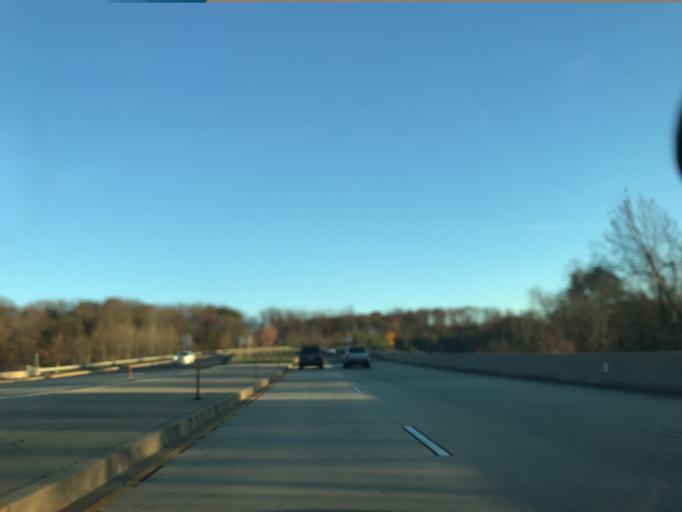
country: US
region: Maryland
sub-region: Baltimore County
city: White Marsh
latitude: 39.3723
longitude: -76.4300
